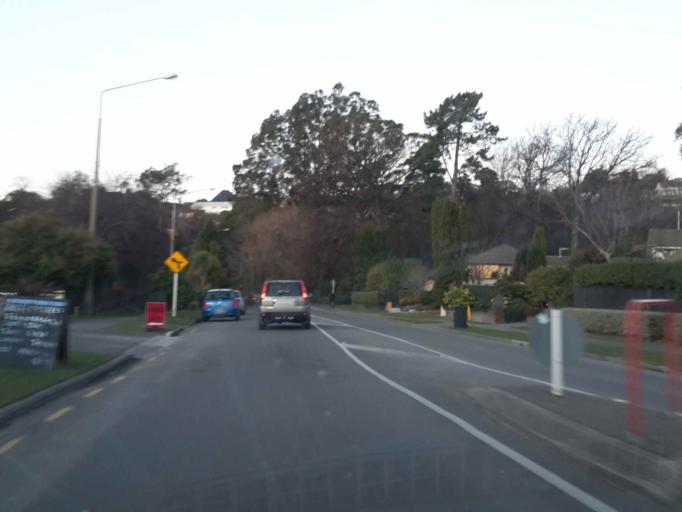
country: NZ
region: Canterbury
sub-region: Christchurch City
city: Christchurch
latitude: -43.5740
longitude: 172.6154
